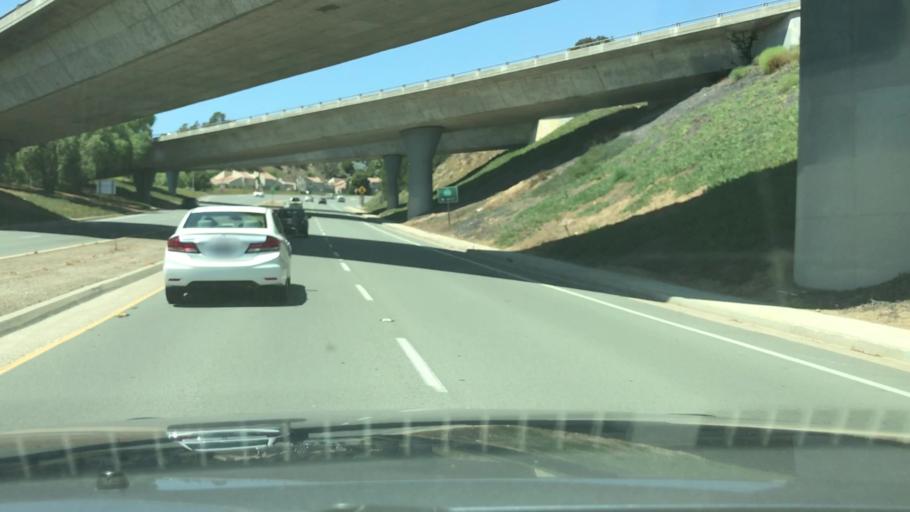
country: US
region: California
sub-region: San Diego County
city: La Jolla
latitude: 32.8464
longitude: -117.2016
